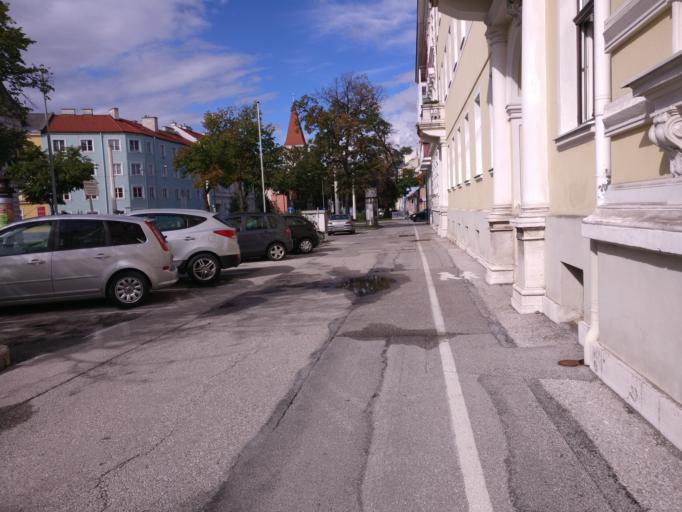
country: AT
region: Lower Austria
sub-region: Wiener Neustadt Stadt
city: Wiener Neustadt
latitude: 47.8109
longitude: 16.2369
